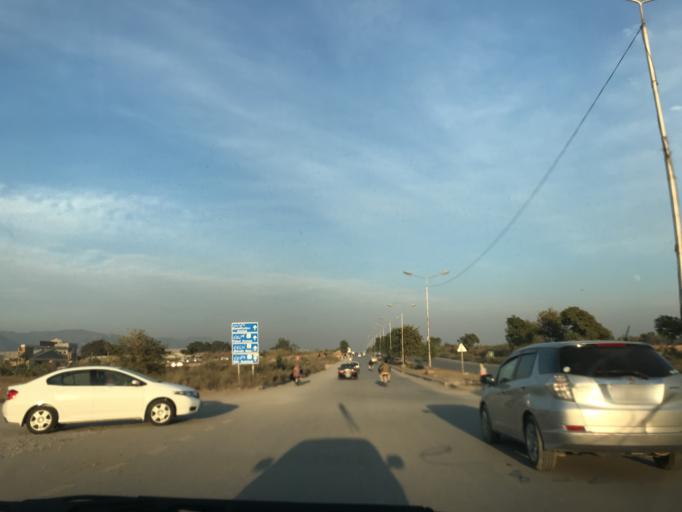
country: PK
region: Islamabad
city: Islamabad
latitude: 33.6911
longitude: 72.9845
